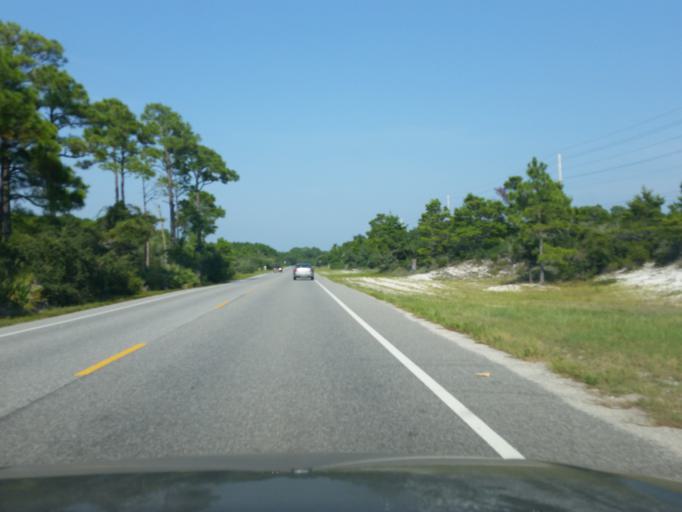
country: US
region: Alabama
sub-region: Baldwin County
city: Gulf Shores
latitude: 30.2381
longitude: -87.9034
